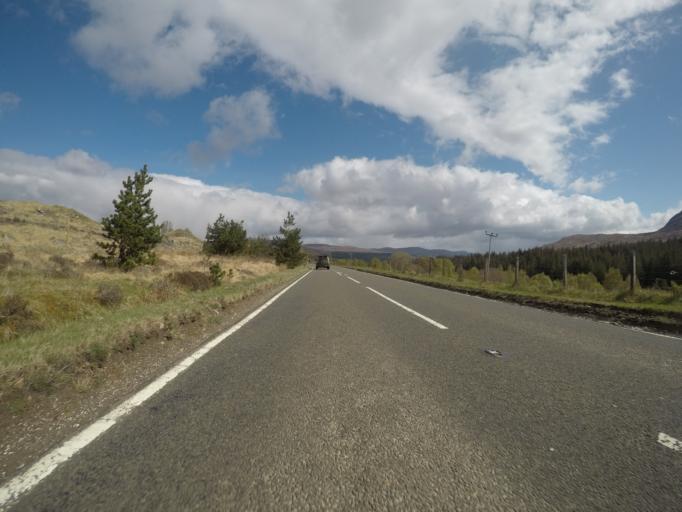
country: GB
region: Scotland
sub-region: Highland
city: Spean Bridge
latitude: 57.1400
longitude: -4.9527
